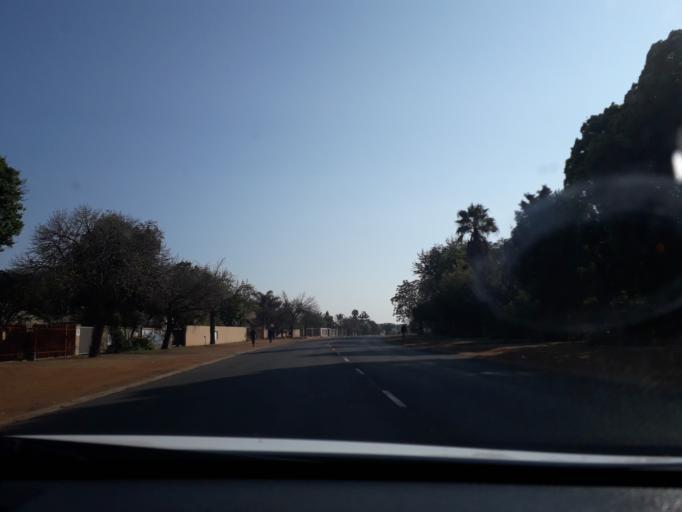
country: ZA
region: Gauteng
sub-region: City of Johannesburg Metropolitan Municipality
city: Modderfontein
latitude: -26.0965
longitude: 28.2412
